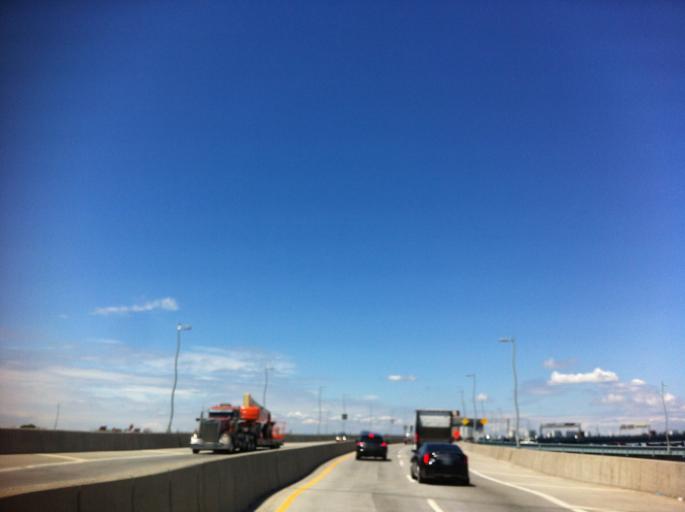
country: US
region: New York
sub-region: Nassau County
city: East Atlantic Beach
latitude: 40.7626
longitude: -73.7789
